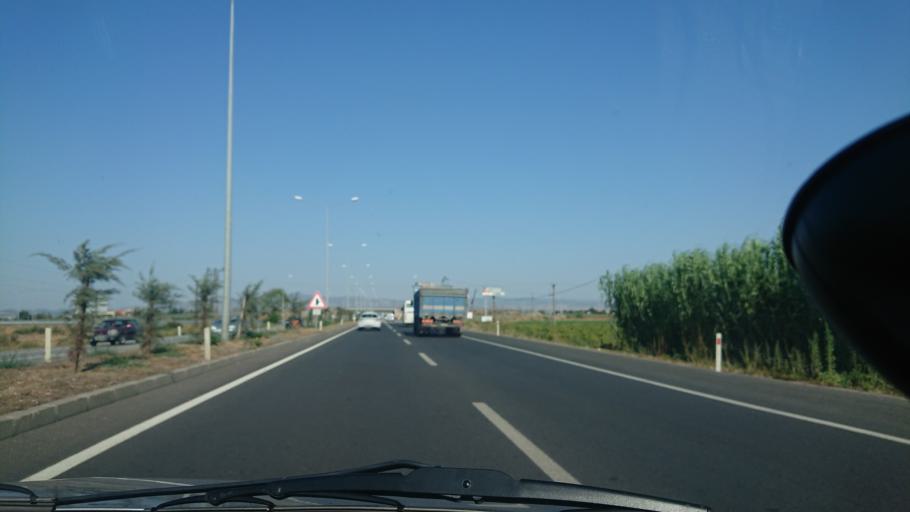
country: TR
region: Manisa
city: Salihli
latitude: 38.4985
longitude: 28.1972
